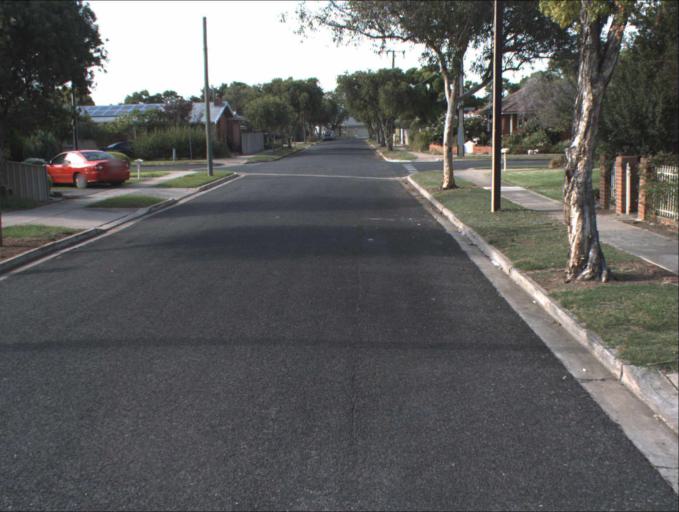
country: AU
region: South Australia
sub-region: Port Adelaide Enfield
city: Klemzig
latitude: -34.8741
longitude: 138.6233
